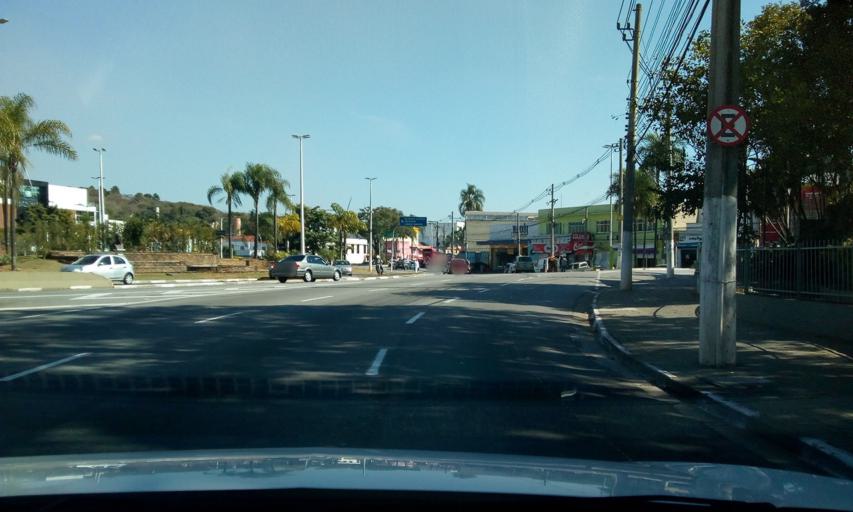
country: BR
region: Sao Paulo
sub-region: Barueri
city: Barueri
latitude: -23.5103
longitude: -46.8728
